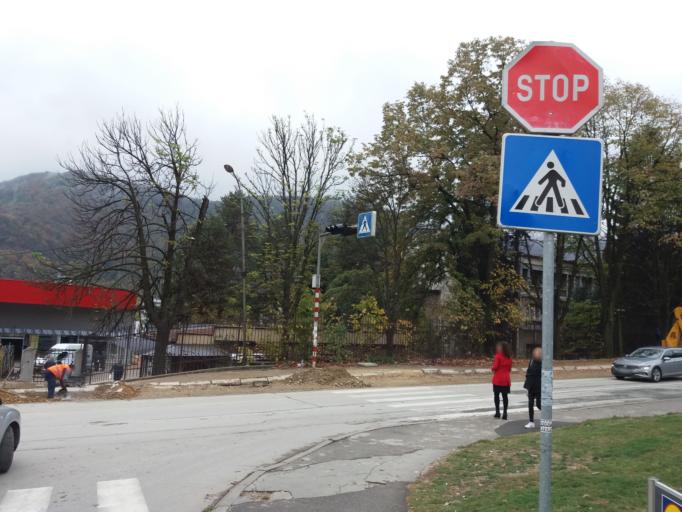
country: RS
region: Central Serbia
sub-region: Zlatiborski Okrug
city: Uzice
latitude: 43.8522
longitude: 19.8561
